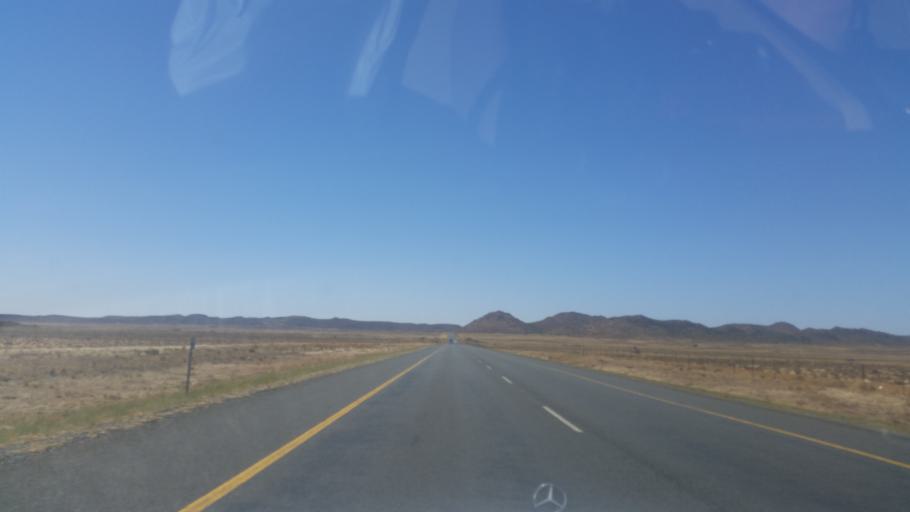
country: ZA
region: Northern Cape
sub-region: Pixley ka Seme District Municipality
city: Colesberg
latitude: -30.6753
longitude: 25.1699
